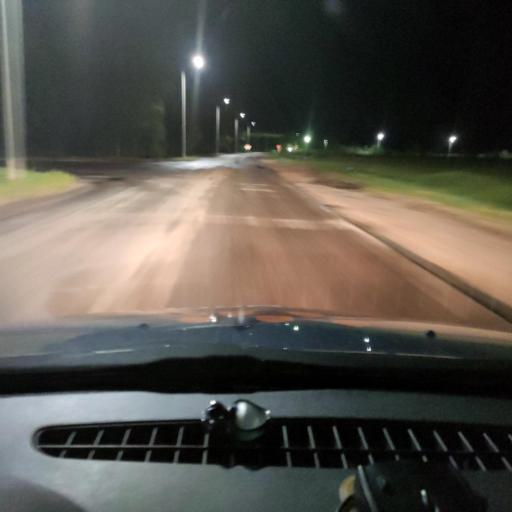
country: RU
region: Voronezj
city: Khrenovoye
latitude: 51.1158
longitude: 40.2646
